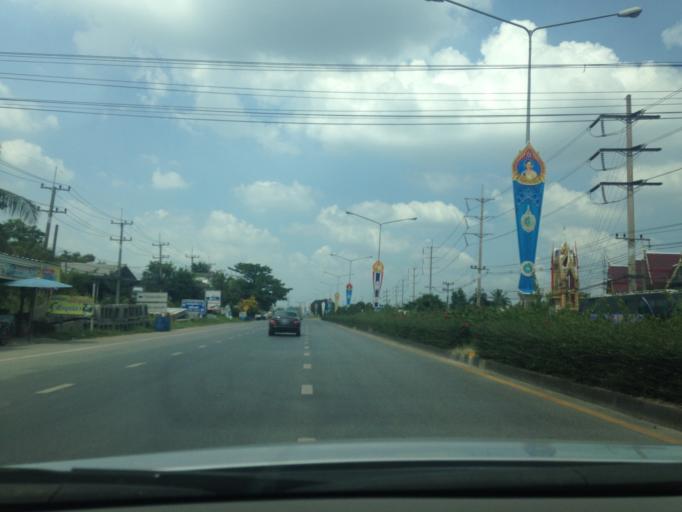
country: TH
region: Pathum Thani
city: Sam Khok
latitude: 14.0780
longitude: 100.5207
